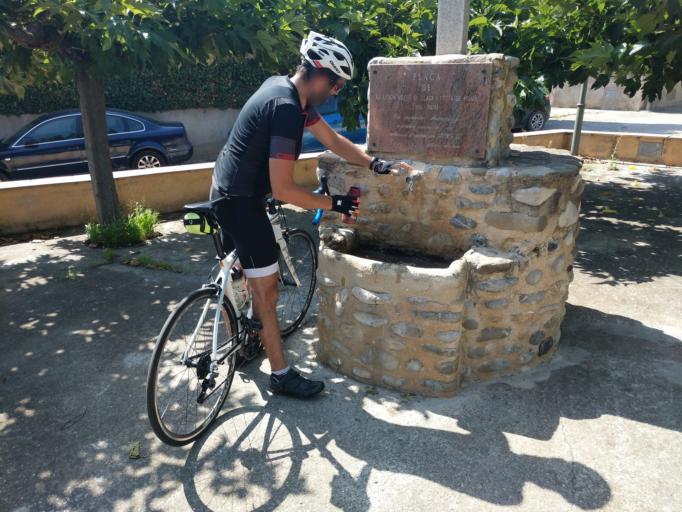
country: ES
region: Catalonia
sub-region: Provincia de Girona
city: Cornella del Terri
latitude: 42.1116
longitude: 2.8520
